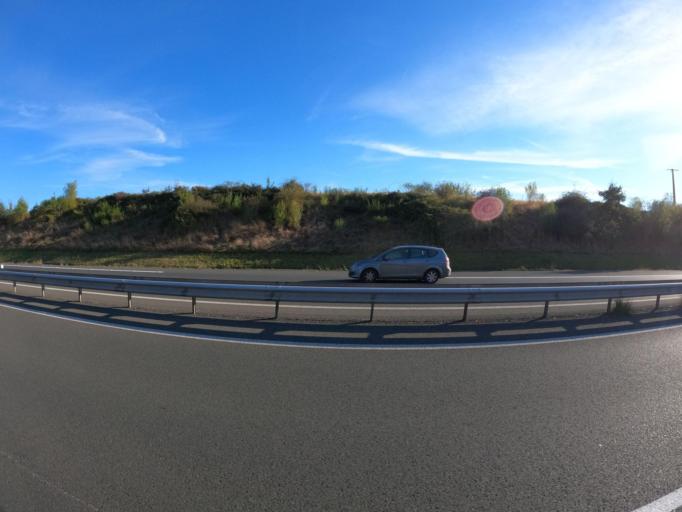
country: FR
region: Pays de la Loire
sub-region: Departement de Maine-et-Loire
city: Saint-Lambert-du-Lattay
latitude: 47.2413
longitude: -0.6453
